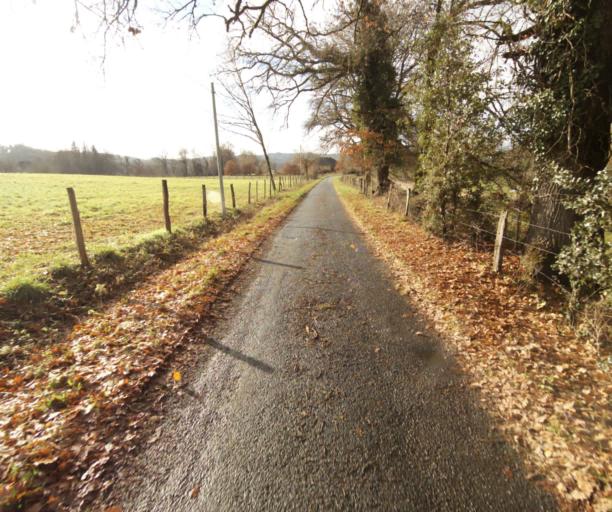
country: FR
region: Limousin
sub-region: Departement de la Correze
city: Sainte-Fereole
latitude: 45.2612
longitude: 1.5992
